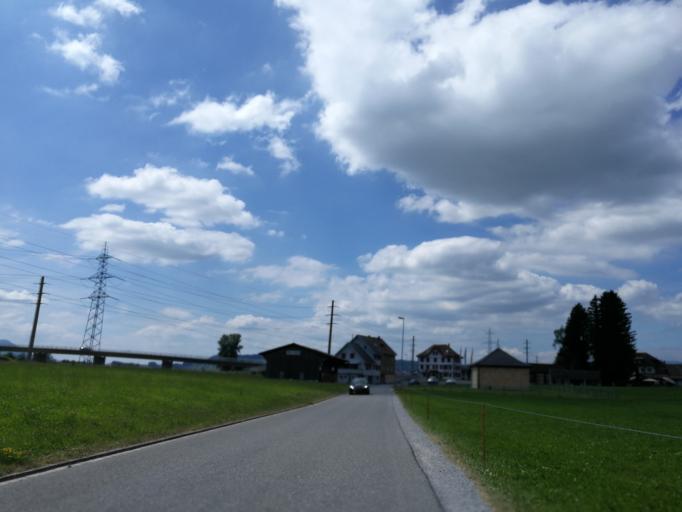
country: CH
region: Saint Gallen
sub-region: Wahlkreis See-Gaster
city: Benken
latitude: 47.1825
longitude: 8.9961
